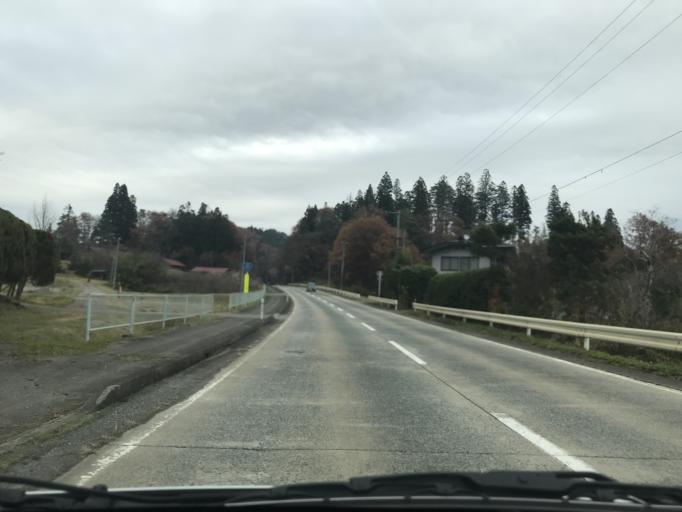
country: JP
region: Iwate
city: Kitakami
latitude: 39.2994
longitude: 141.1990
